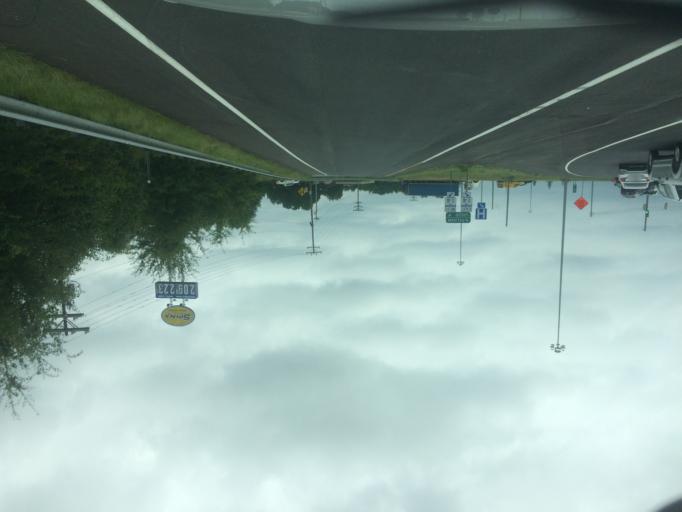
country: US
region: South Carolina
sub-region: Greenville County
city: Greer
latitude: 34.8732
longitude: -82.2234
